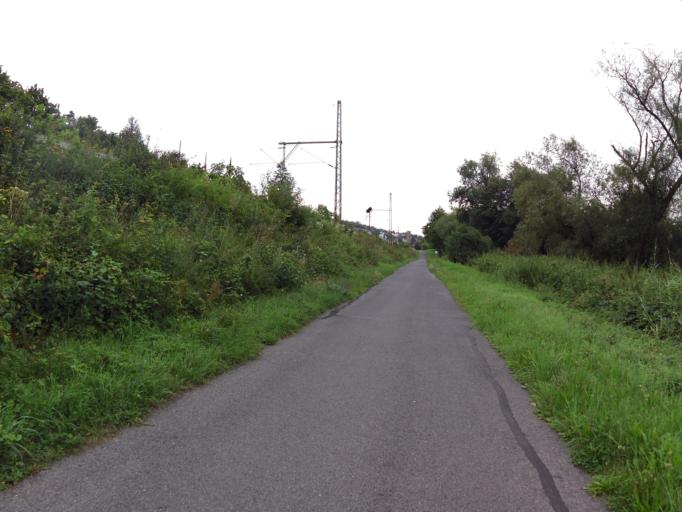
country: DE
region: Bavaria
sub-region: Regierungsbezirk Unterfranken
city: Schonungen
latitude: 50.0527
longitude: 10.2973
